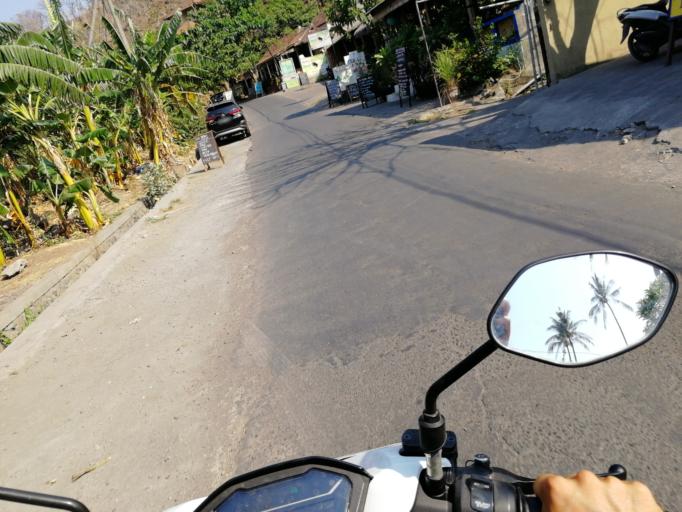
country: ID
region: Bali
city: Biaslantang Kaler
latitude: -8.3512
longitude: 115.6828
